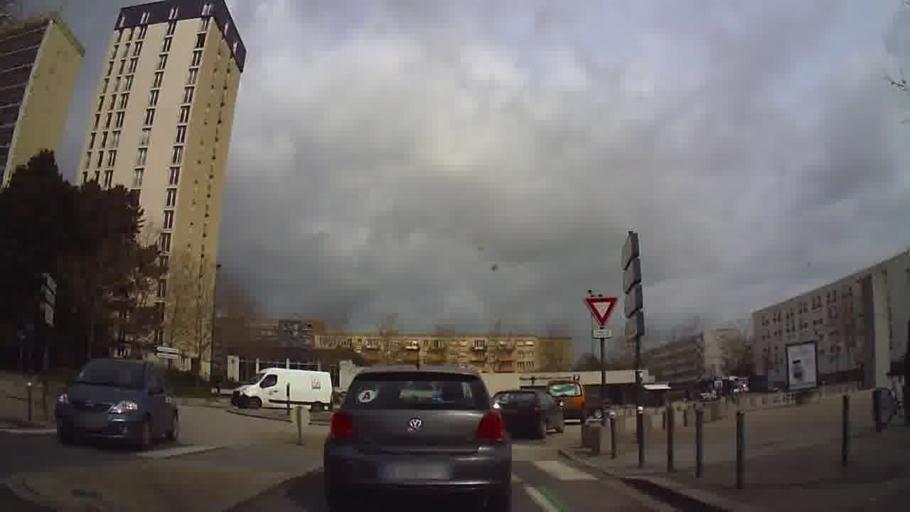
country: FR
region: Brittany
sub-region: Departement d'Ille-et-Vilaine
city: Rennes
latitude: 48.1210
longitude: -1.7044
